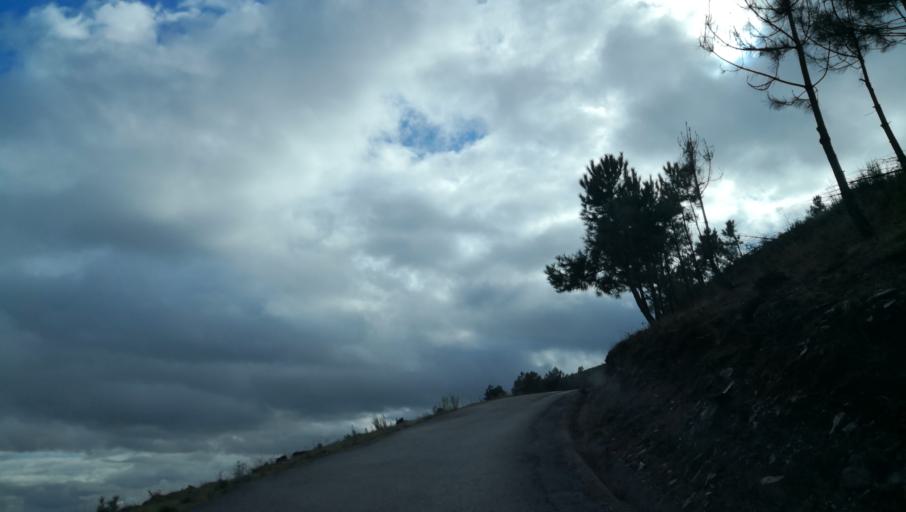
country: PT
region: Vila Real
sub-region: Sabrosa
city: Vilela
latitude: 41.1998
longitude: -7.5781
